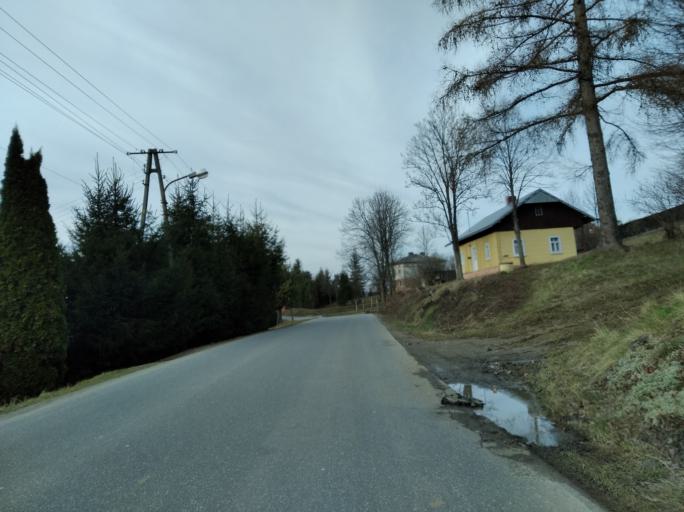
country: PL
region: Subcarpathian Voivodeship
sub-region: Powiat brzozowski
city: Gorki
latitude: 49.6492
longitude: 22.0359
